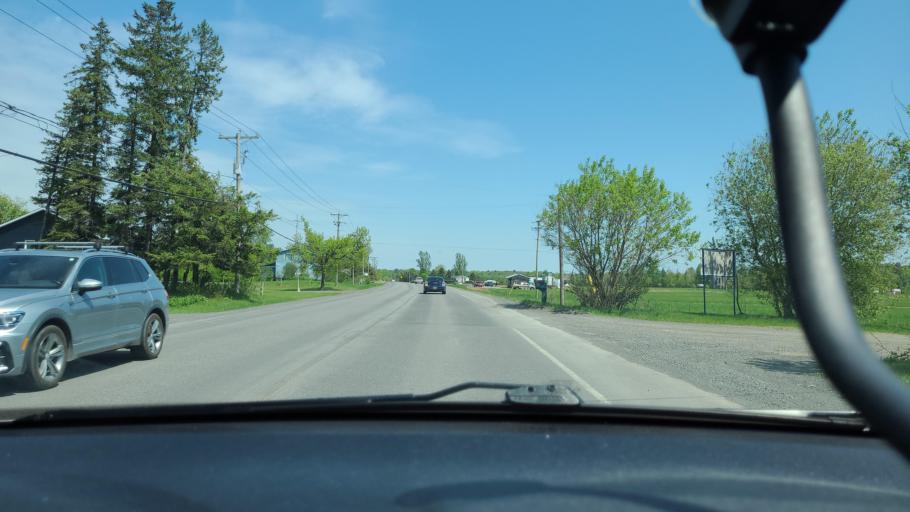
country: CA
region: Quebec
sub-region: Laurentides
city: Lachute
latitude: 45.6677
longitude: -74.2301
